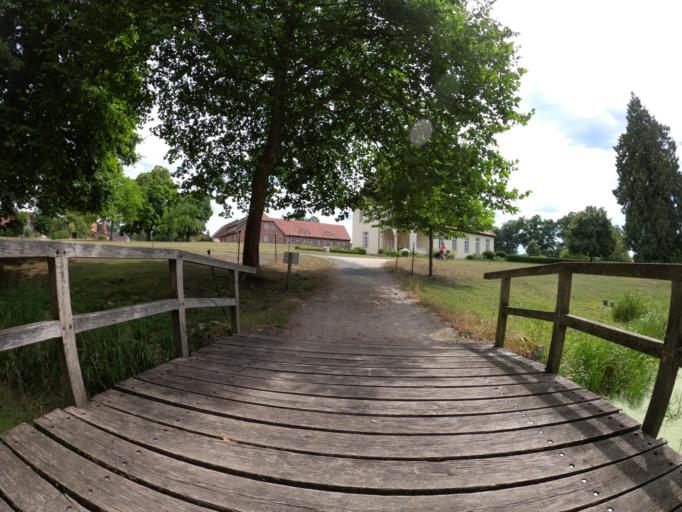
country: DE
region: Mecklenburg-Vorpommern
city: Loitz
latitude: 53.4037
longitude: 13.4485
